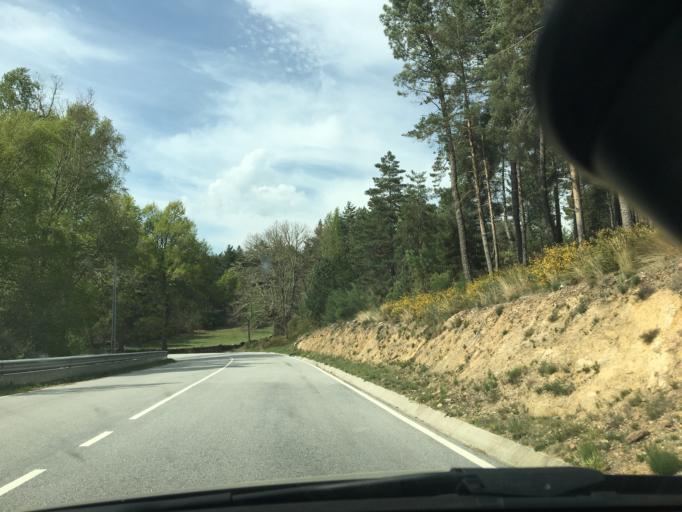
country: PT
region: Vila Real
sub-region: Boticas
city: Boticas
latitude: 41.6841
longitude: -7.7205
